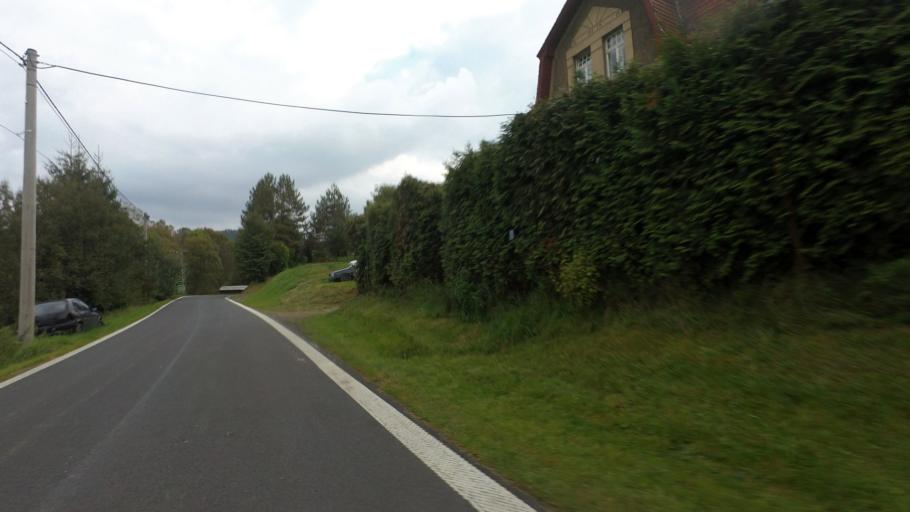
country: CZ
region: Ustecky
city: Dolni Poustevna
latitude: 50.9961
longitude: 14.2915
